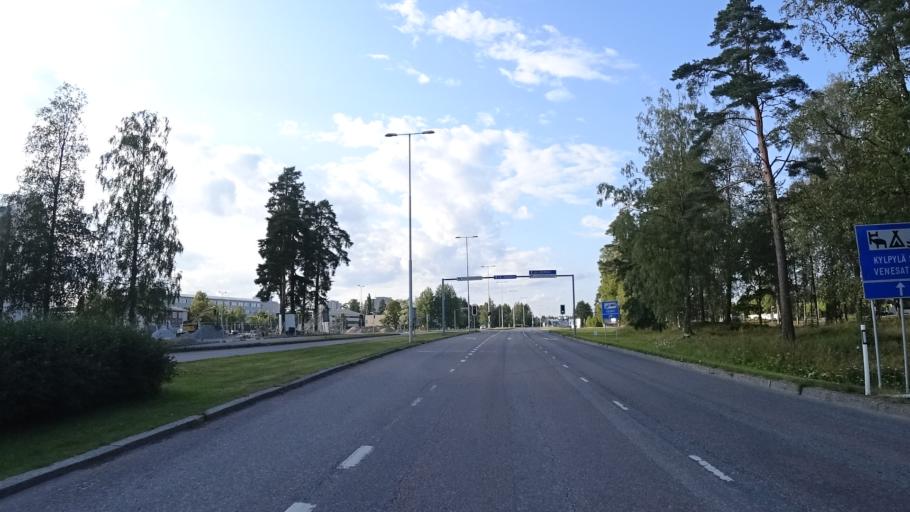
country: FI
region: South Karelia
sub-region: Imatra
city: Imatra
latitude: 61.1838
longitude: 28.7797
